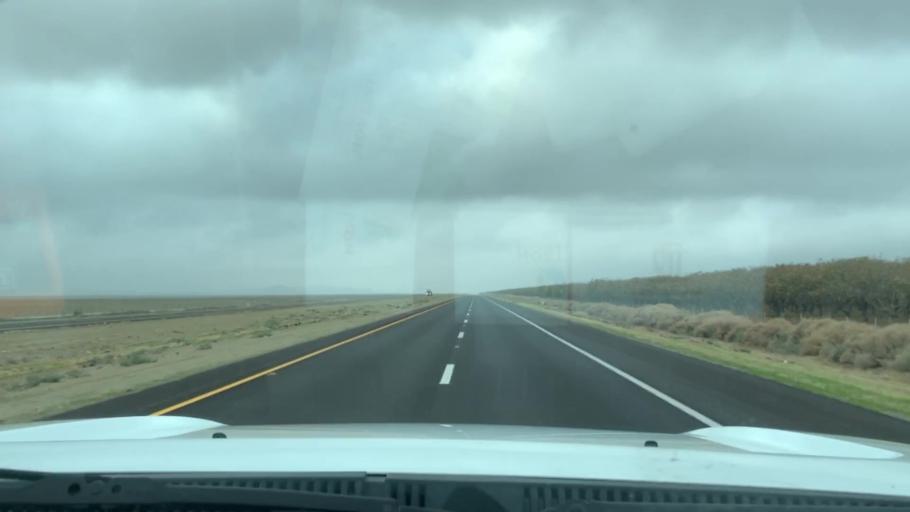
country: US
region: California
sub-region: Kern County
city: Lost Hills
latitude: 35.6148
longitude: -119.9063
